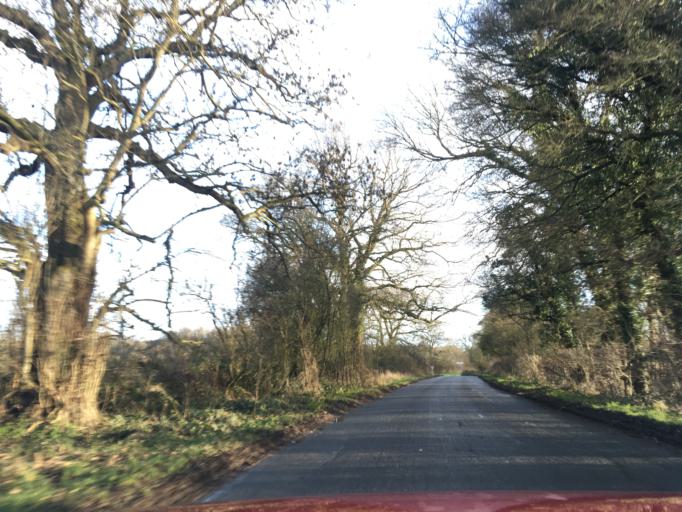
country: GB
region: England
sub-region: Warwickshire
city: Henley in Arden
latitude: 52.2214
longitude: -1.7877
